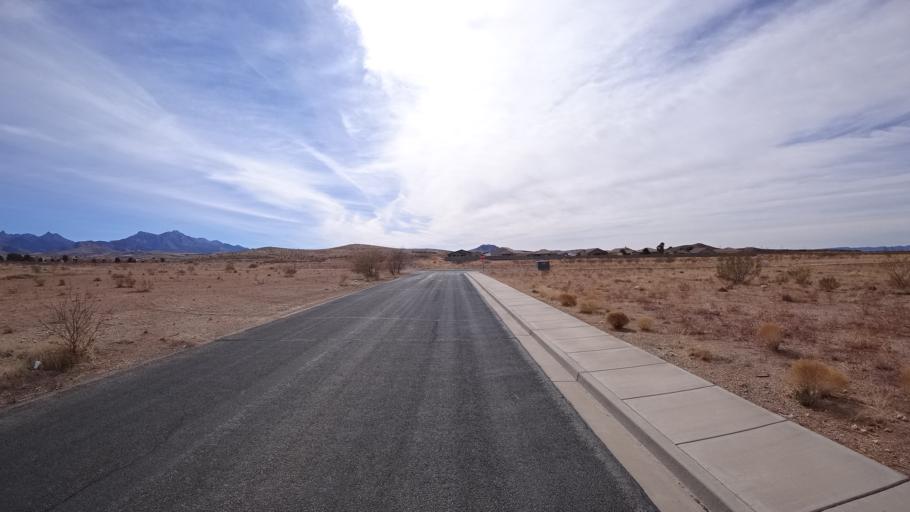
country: US
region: Arizona
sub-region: Mohave County
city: Kingman
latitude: 35.1892
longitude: -114.0159
